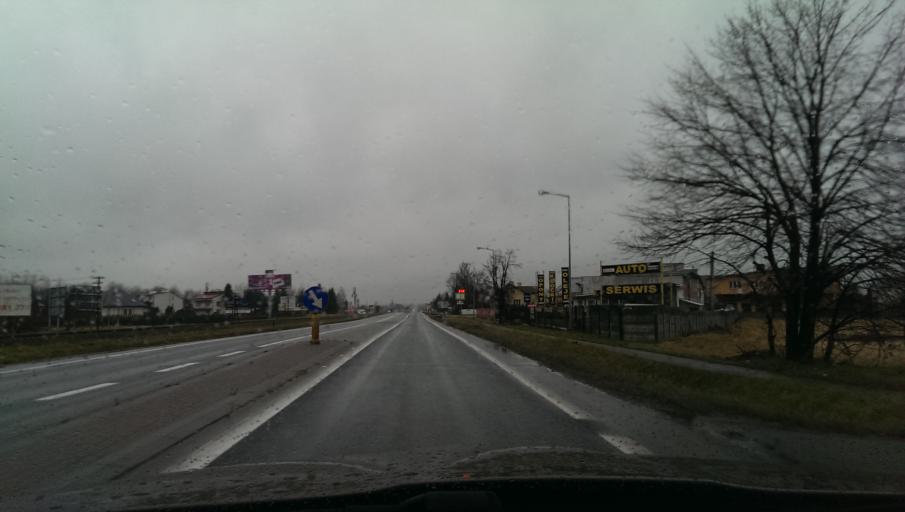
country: PL
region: Subcarpathian Voivodeship
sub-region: Powiat rzeszowski
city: Rudna Mala
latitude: 50.0787
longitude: 21.9864
